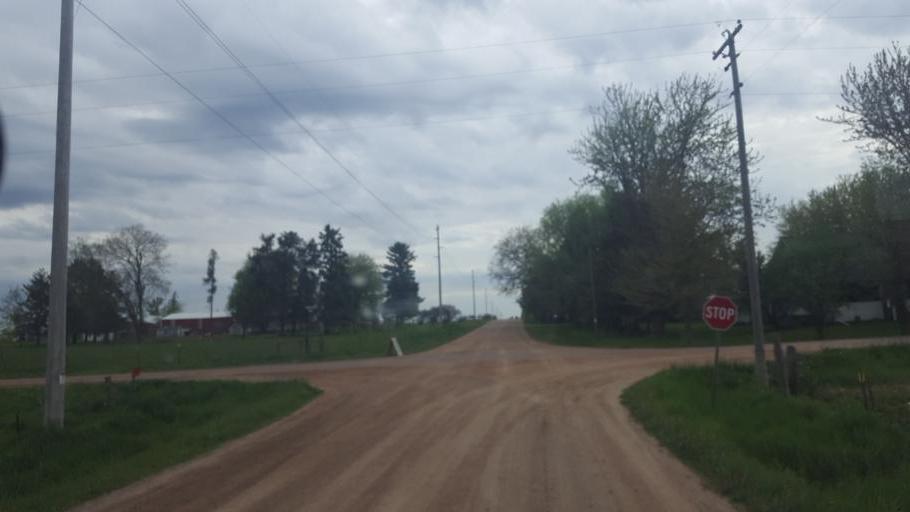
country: US
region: Wisconsin
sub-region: Marathon County
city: Spencer
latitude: 44.6261
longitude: -90.3766
